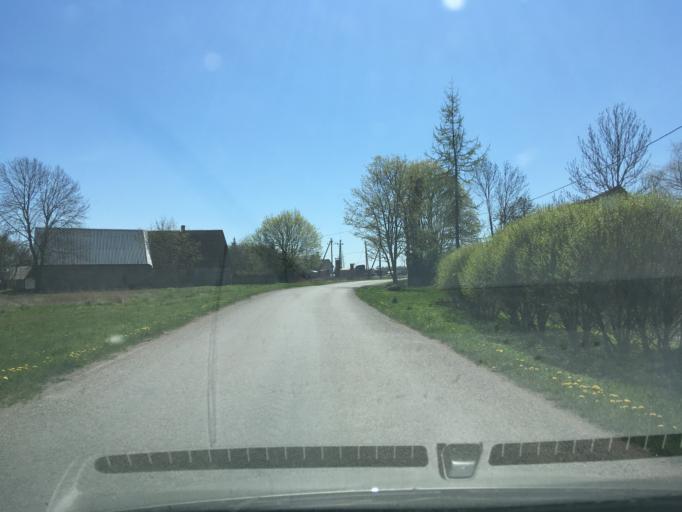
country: EE
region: Harju
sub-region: Raasiku vald
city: Arukula
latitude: 59.3906
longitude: 25.0804
